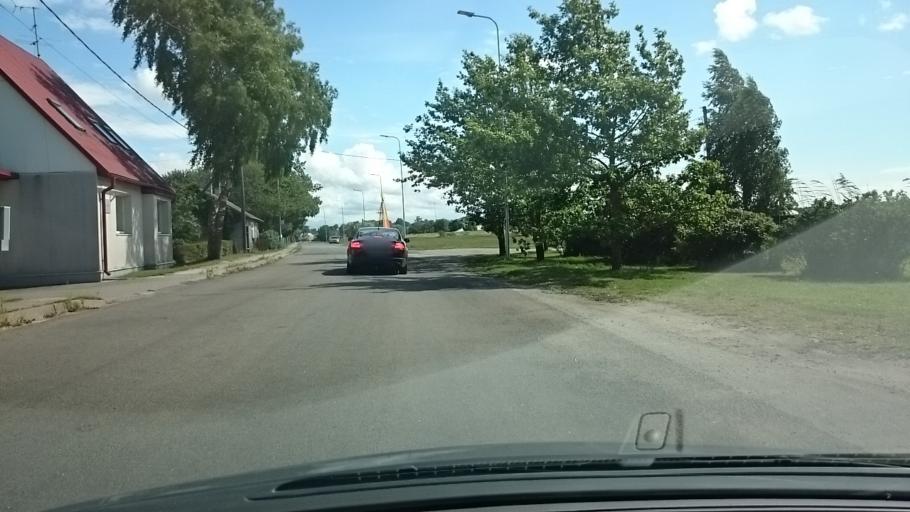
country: EE
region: Laeaene
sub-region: Haapsalu linn
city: Haapsalu
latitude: 58.9542
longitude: 23.5224
